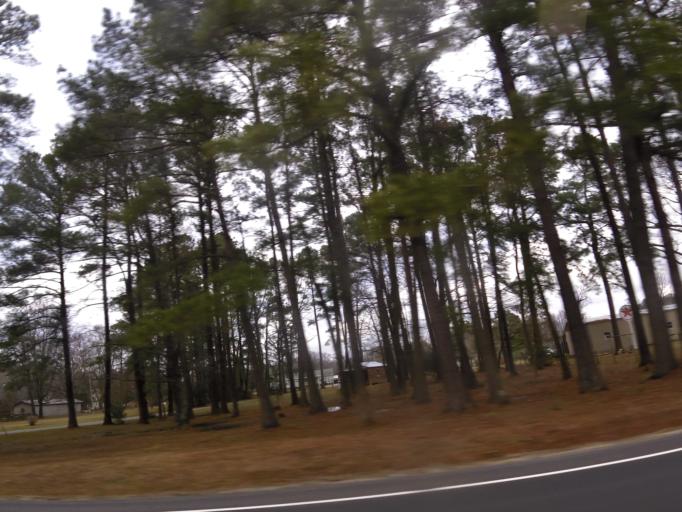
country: US
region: North Carolina
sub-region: Nash County
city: Rocky Mount
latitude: 35.8653
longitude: -77.7237
